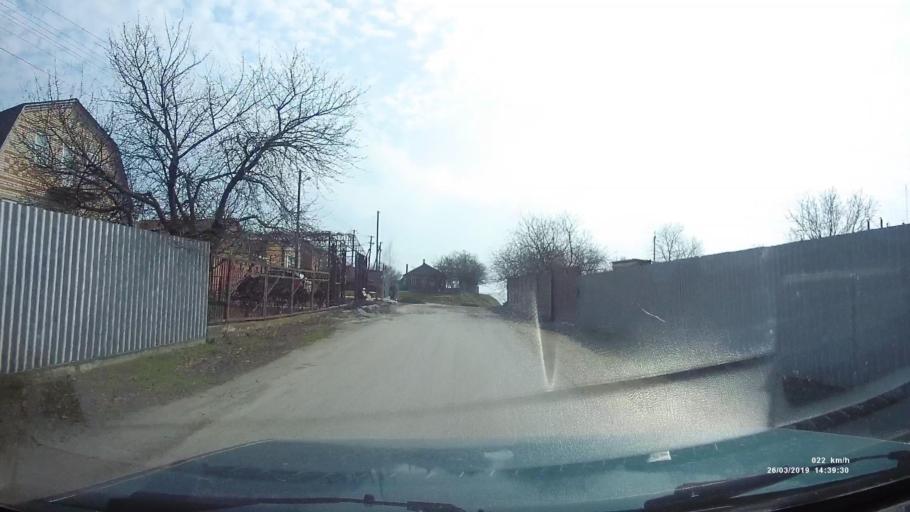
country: RU
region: Rostov
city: Novobessergenovka
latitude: 47.1779
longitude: 38.8628
